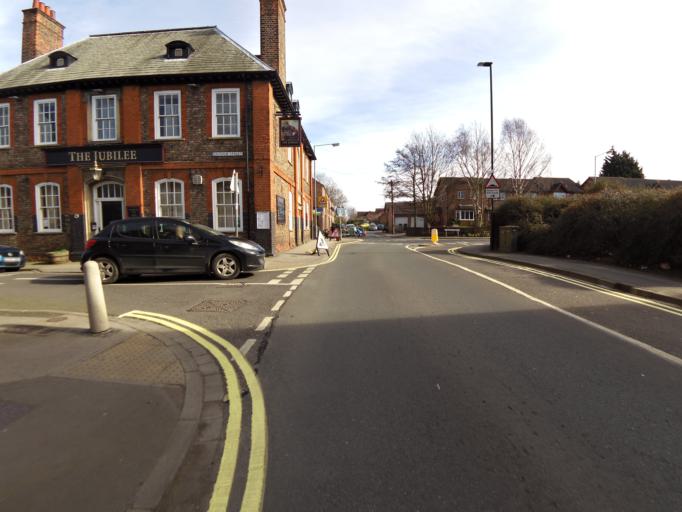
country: GB
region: England
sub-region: City of York
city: York
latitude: 53.9642
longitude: -1.1050
